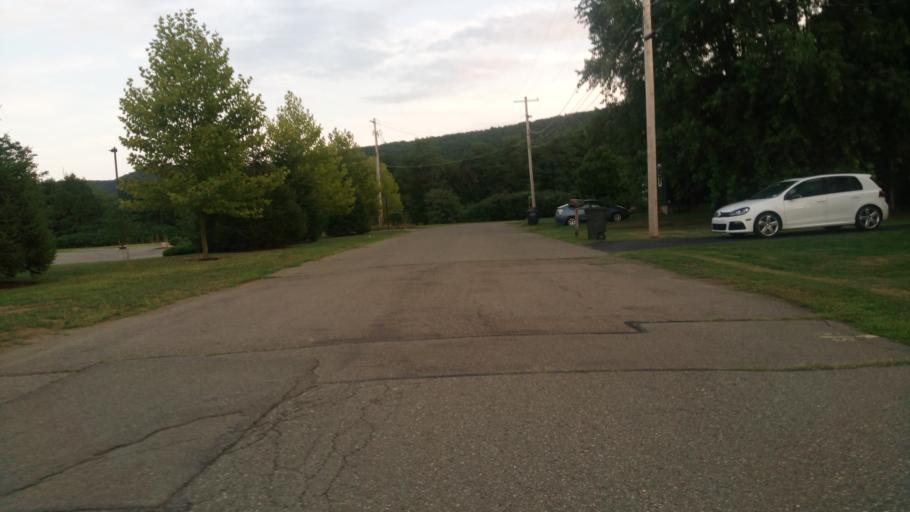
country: US
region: New York
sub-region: Chemung County
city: Southport
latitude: 42.0585
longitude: -76.8093
